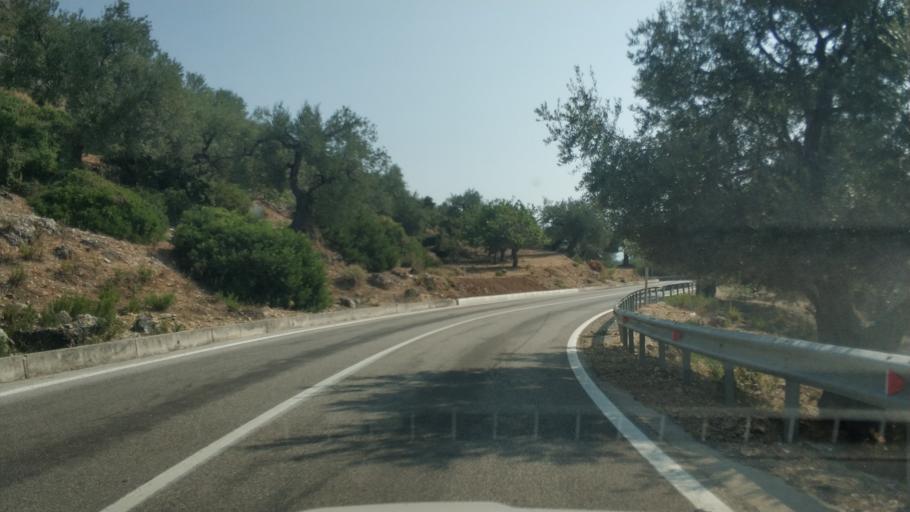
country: AL
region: Vlore
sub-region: Rrethi i Sarandes
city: Lukove
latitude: 40.0242
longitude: 19.8863
